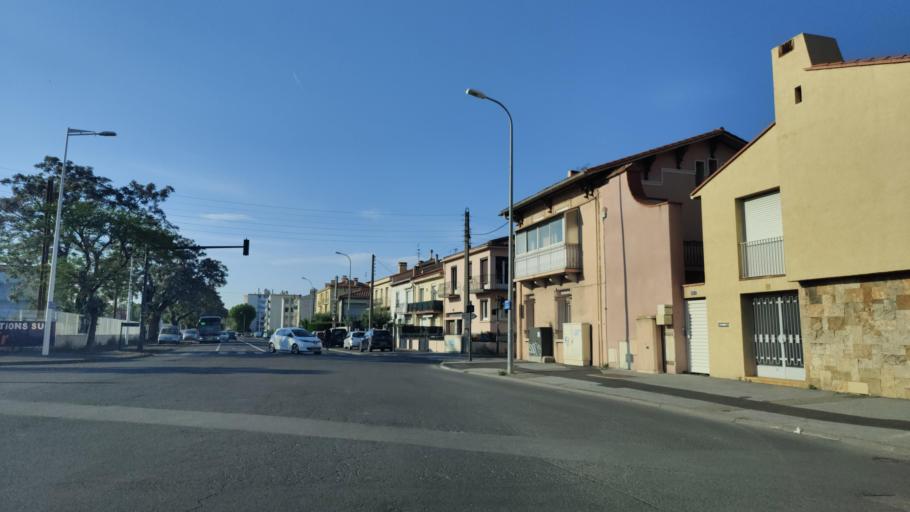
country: FR
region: Languedoc-Roussillon
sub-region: Departement des Pyrenees-Orientales
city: Perpignan
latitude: 42.7075
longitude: 2.8865
